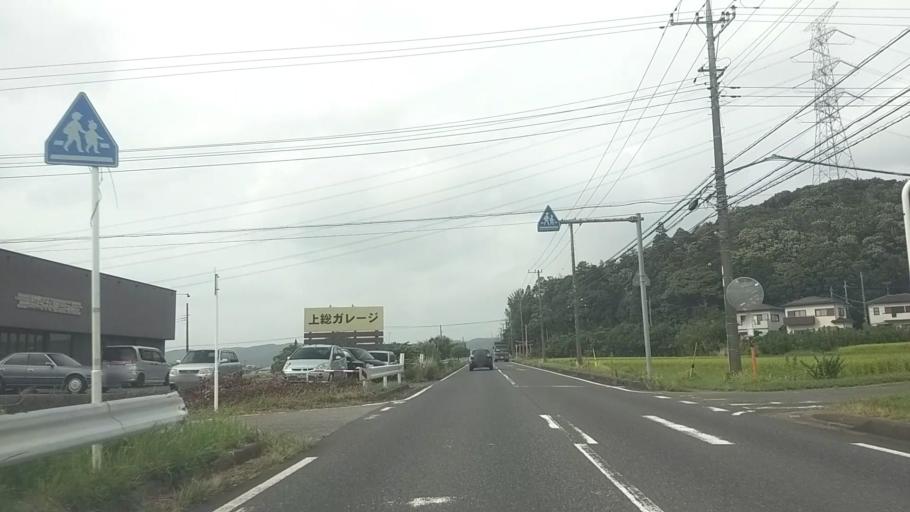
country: JP
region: Chiba
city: Kimitsu
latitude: 35.2825
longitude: 139.9901
